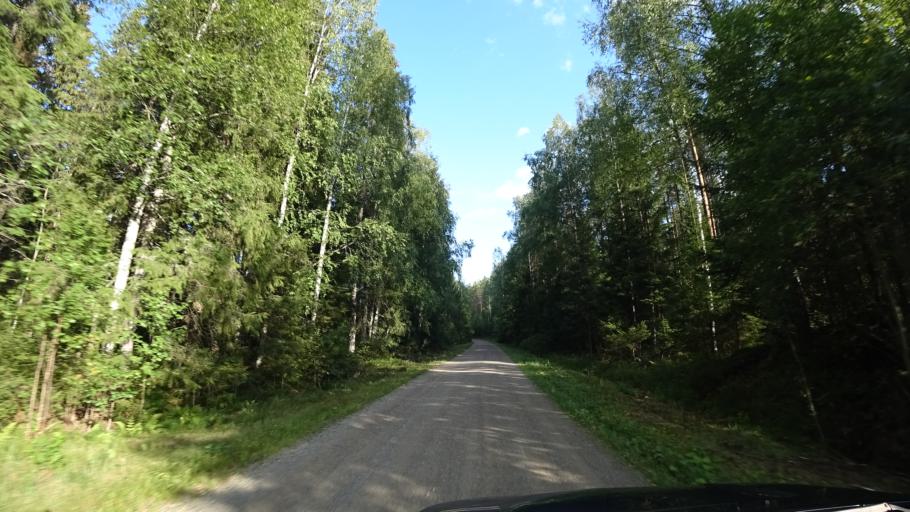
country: FI
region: Paijanne Tavastia
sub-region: Lahti
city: Auttoinen
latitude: 61.2148
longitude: 25.1561
